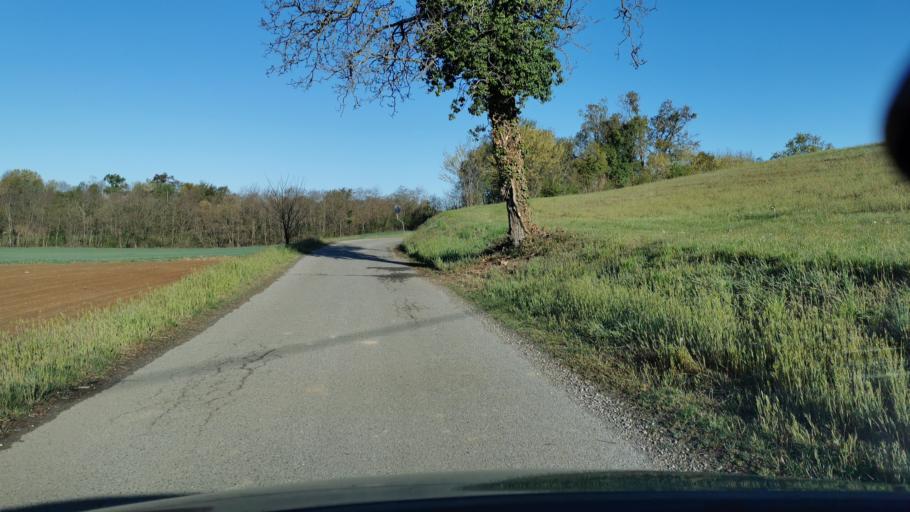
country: IT
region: Piedmont
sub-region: Provincia di Torino
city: Leini
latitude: 45.2124
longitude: 7.7110
